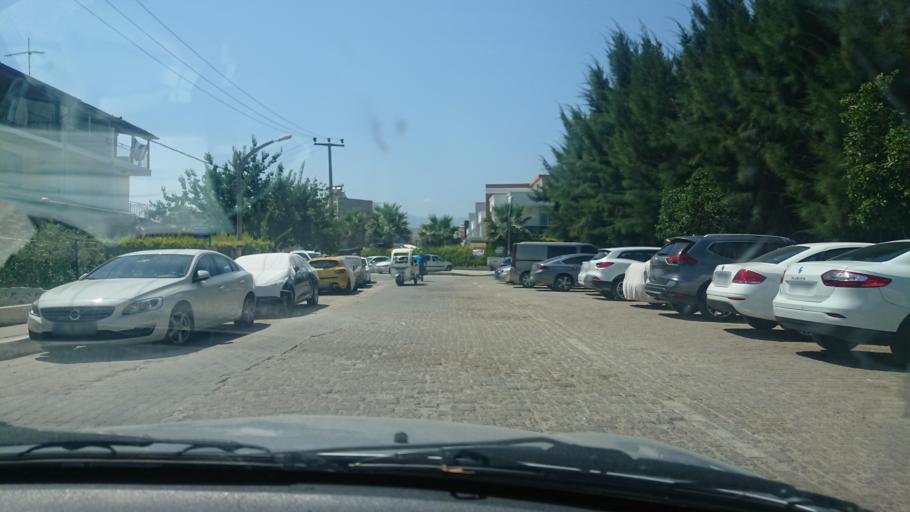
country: TR
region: Aydin
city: Kusadasi
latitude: 37.7998
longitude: 27.2727
